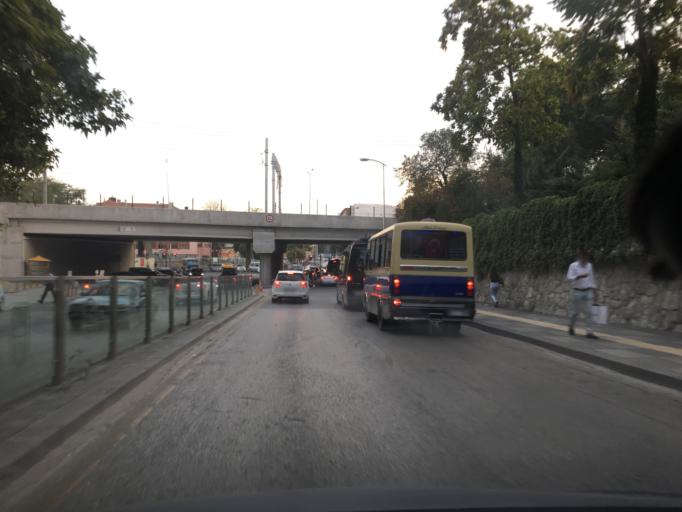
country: TR
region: Ankara
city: Ankara
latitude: 39.9298
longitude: 32.8600
